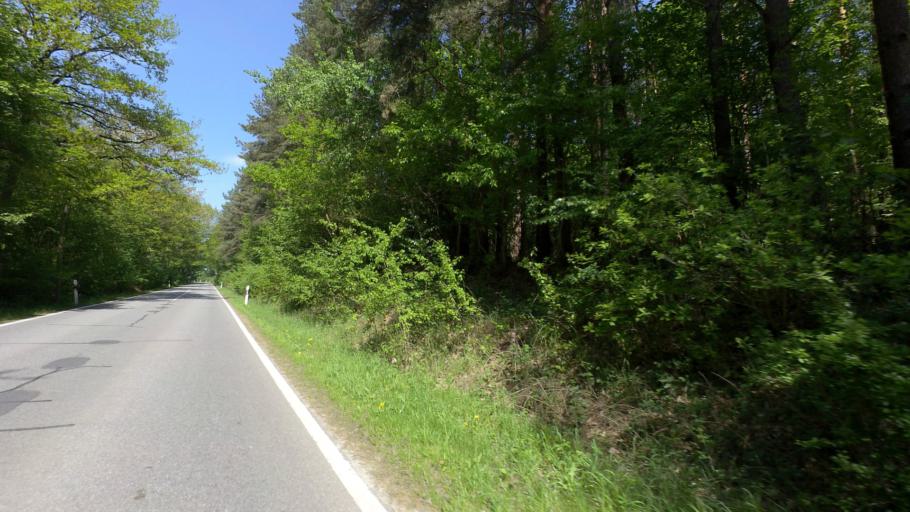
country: DE
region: Mecklenburg-Vorpommern
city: Mollenhagen
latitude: 53.5729
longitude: 12.8953
